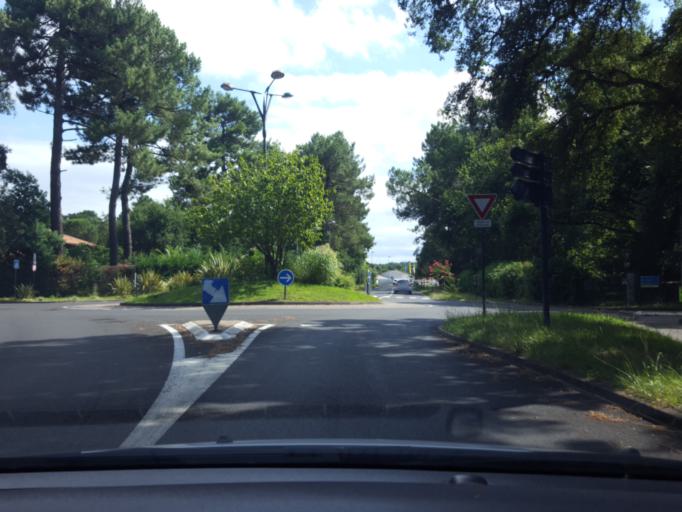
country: FR
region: Aquitaine
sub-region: Departement des Landes
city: Capbreton
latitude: 43.6365
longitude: -1.4264
